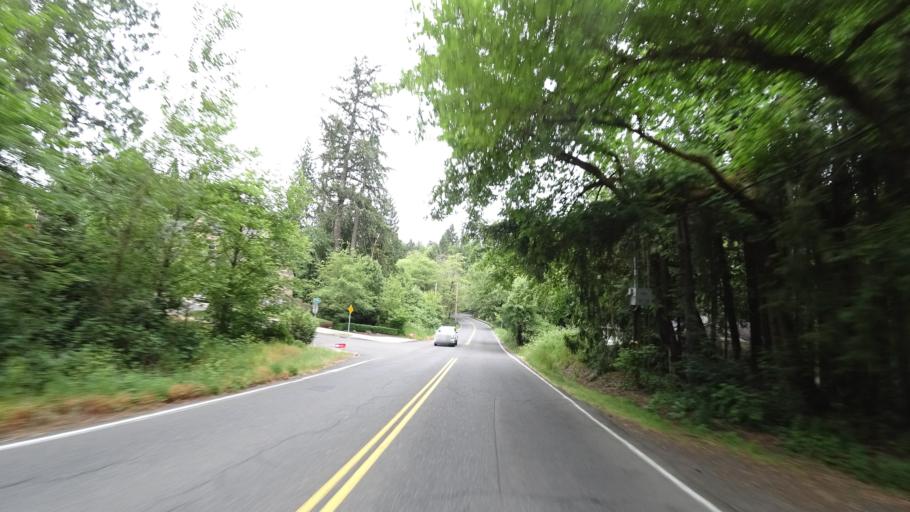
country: US
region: Oregon
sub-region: Clackamas County
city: Lake Oswego
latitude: 45.4483
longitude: -122.6866
